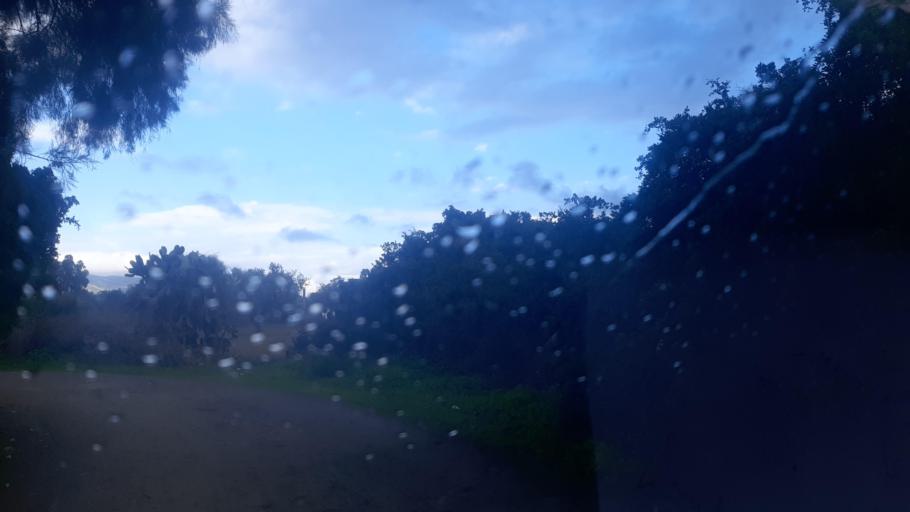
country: TN
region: Nabul
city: Manzil Bu Zalafah
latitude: 36.7377
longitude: 10.5299
